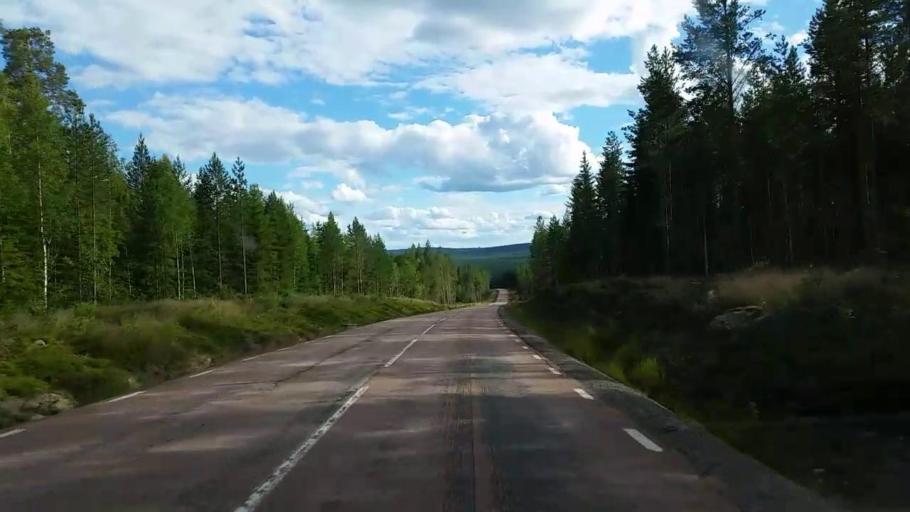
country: SE
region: Gaevleborg
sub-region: Ljusdals Kommun
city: Farila
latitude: 61.9463
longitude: 15.8840
